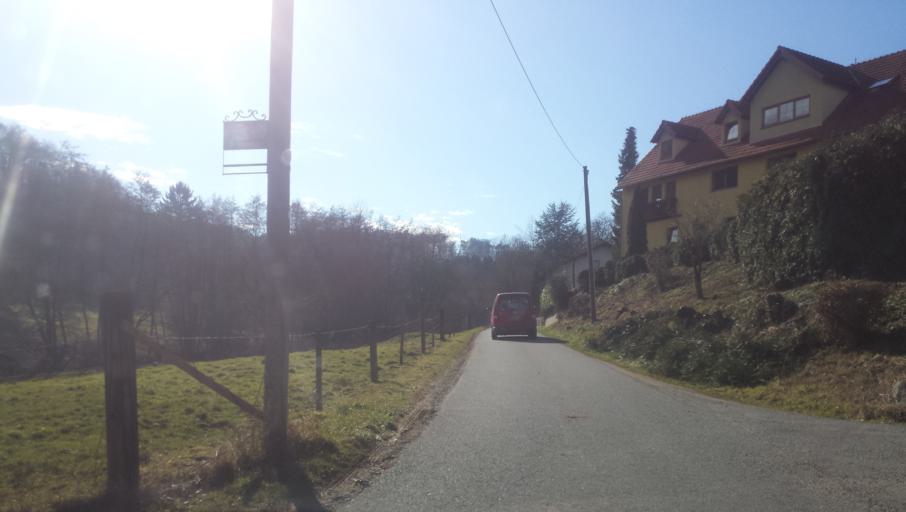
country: DE
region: Hesse
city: Reichelsheim
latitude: 49.7382
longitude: 8.8305
